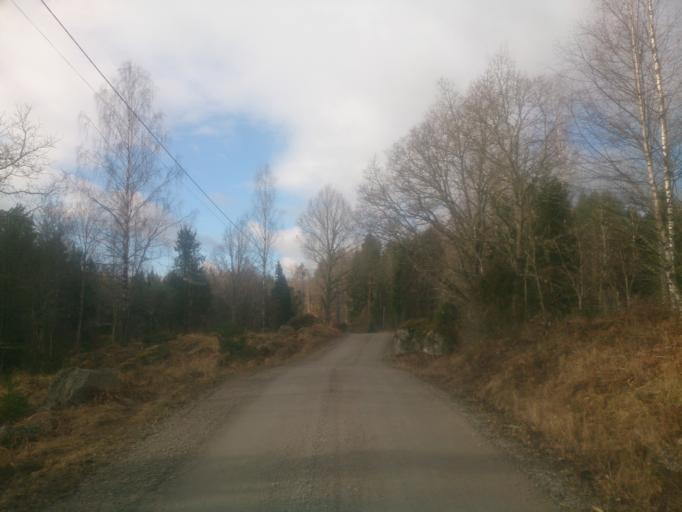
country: SE
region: OEstergoetland
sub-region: Atvidabergs Kommun
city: Atvidaberg
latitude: 58.2247
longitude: 16.1744
